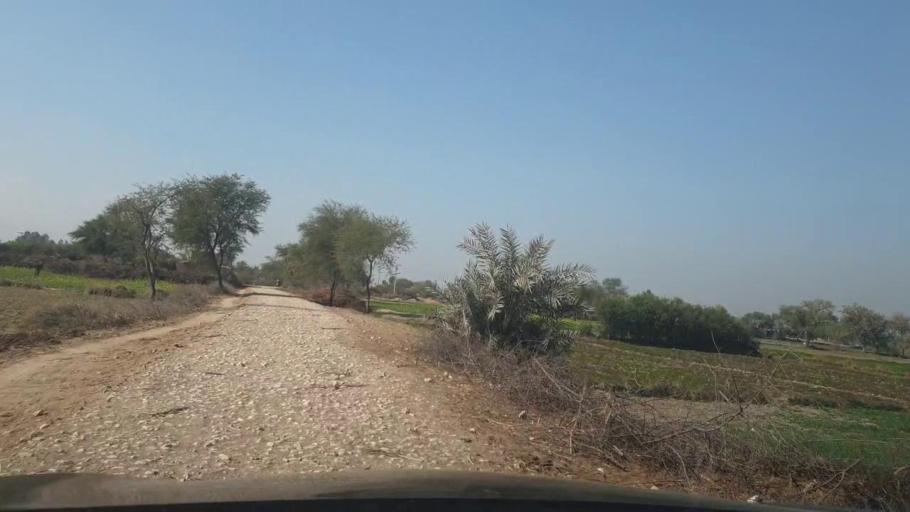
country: PK
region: Sindh
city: Ubauro
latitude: 28.1325
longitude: 69.6773
